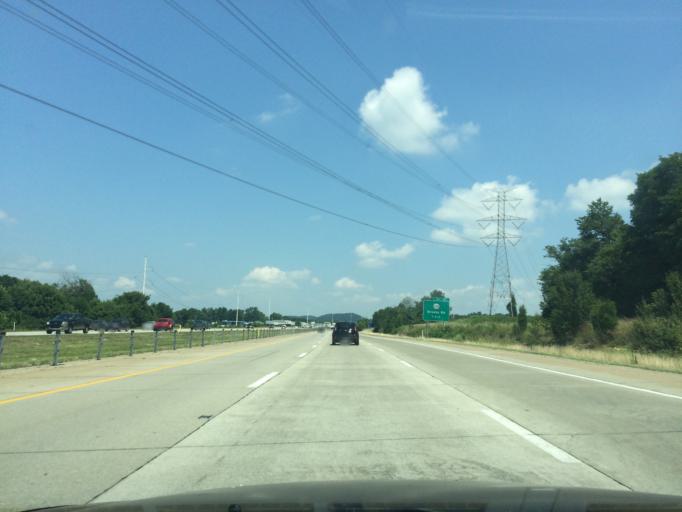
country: US
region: Kentucky
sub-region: Bullitt County
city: Brooks
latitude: 38.0436
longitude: -85.6966
